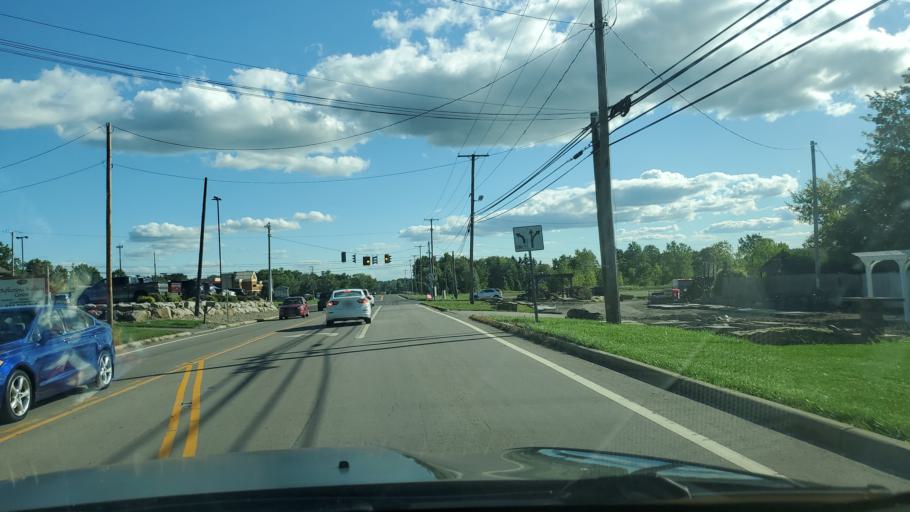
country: US
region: Ohio
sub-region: Mahoning County
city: Canfield
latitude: 41.0451
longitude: -80.7607
